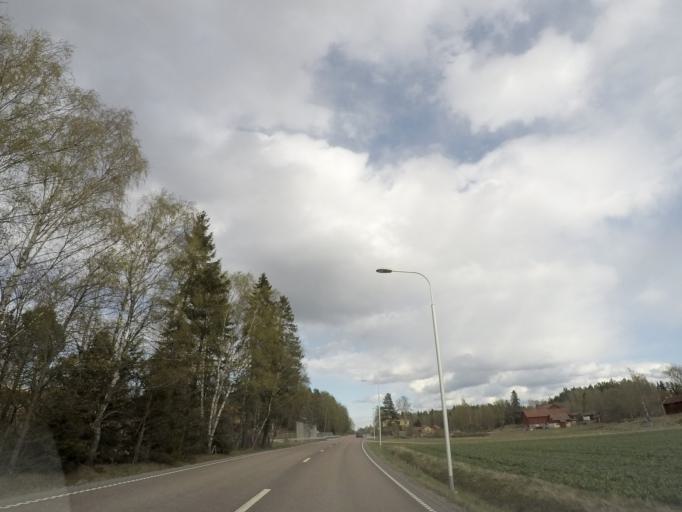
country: SE
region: Soedermanland
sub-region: Eskilstuna Kommun
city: Hallbybrunn
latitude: 59.3206
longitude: 16.3169
